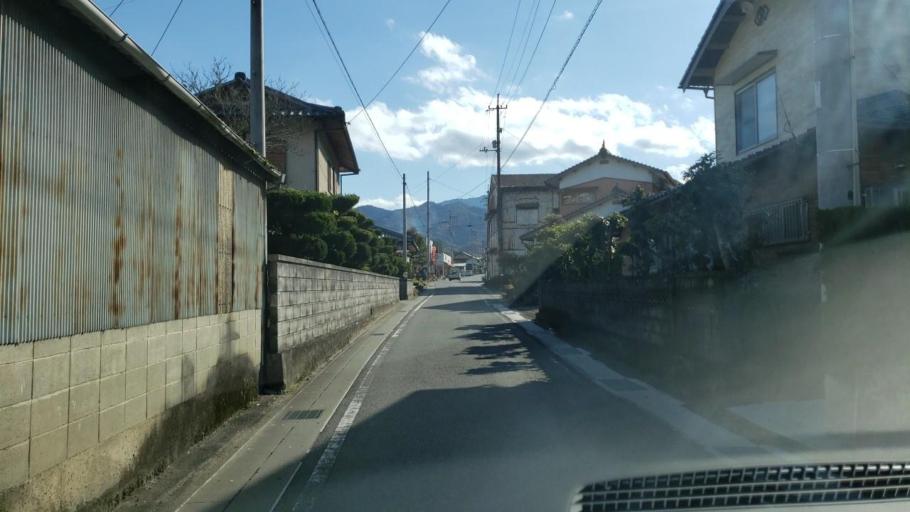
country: JP
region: Tokushima
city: Wakimachi
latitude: 34.0363
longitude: 134.0282
